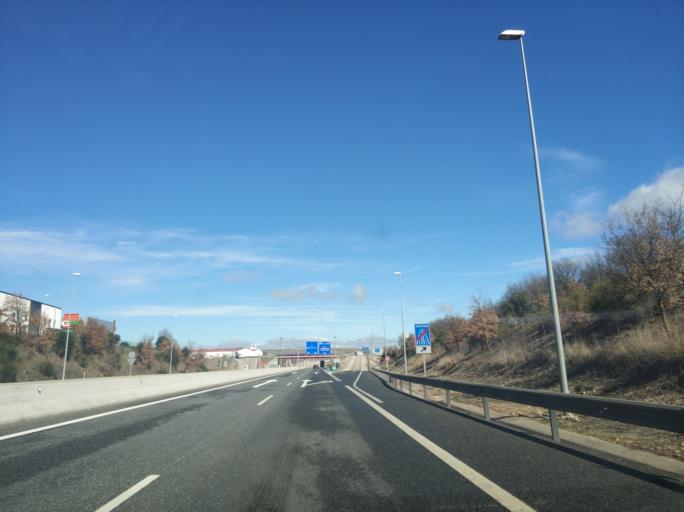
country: ES
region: Castille and Leon
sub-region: Provincia de Burgos
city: Cardenajimeno
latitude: 42.3577
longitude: -3.6385
